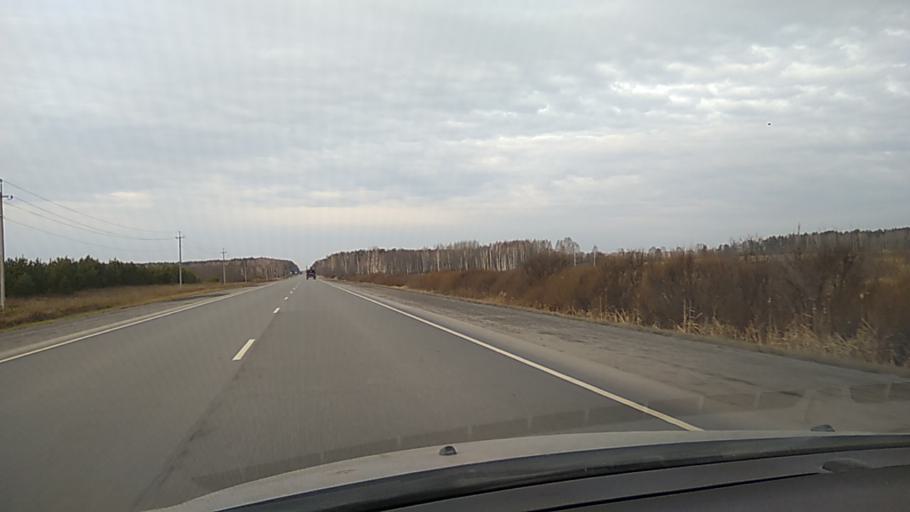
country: RU
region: Sverdlovsk
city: Troitskiy
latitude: 57.0893
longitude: 63.8587
